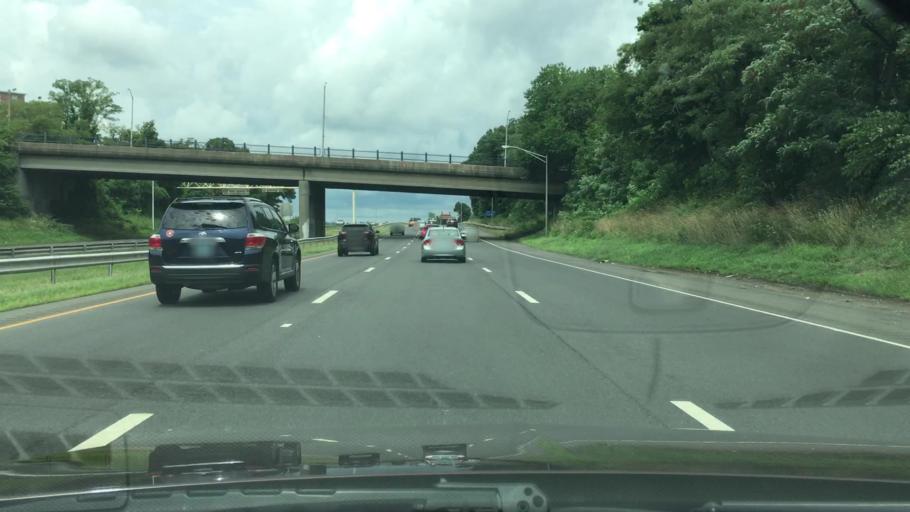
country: US
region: Connecticut
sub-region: Fairfield County
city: Bridgeport
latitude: 41.1822
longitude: -73.1938
